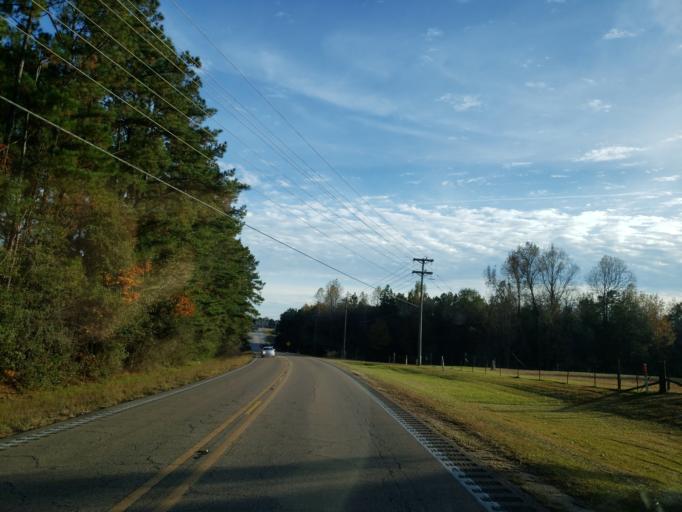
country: US
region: Mississippi
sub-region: Lamar County
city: West Hattiesburg
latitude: 31.2898
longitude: -89.4708
